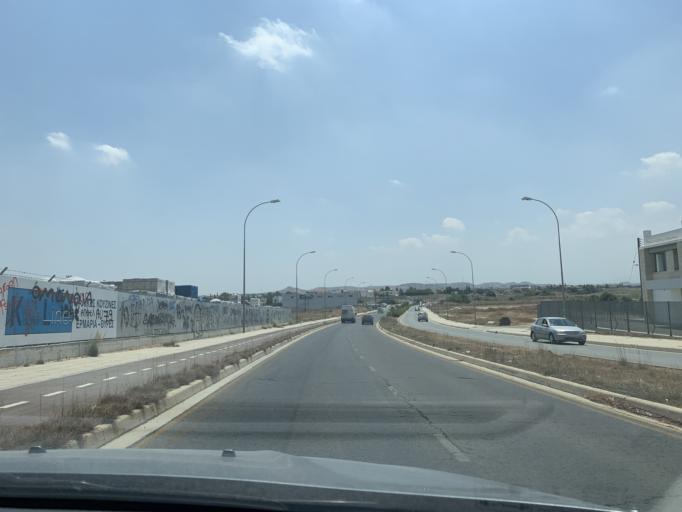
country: CY
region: Lefkosia
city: Nicosia
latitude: 35.1198
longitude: 33.3567
